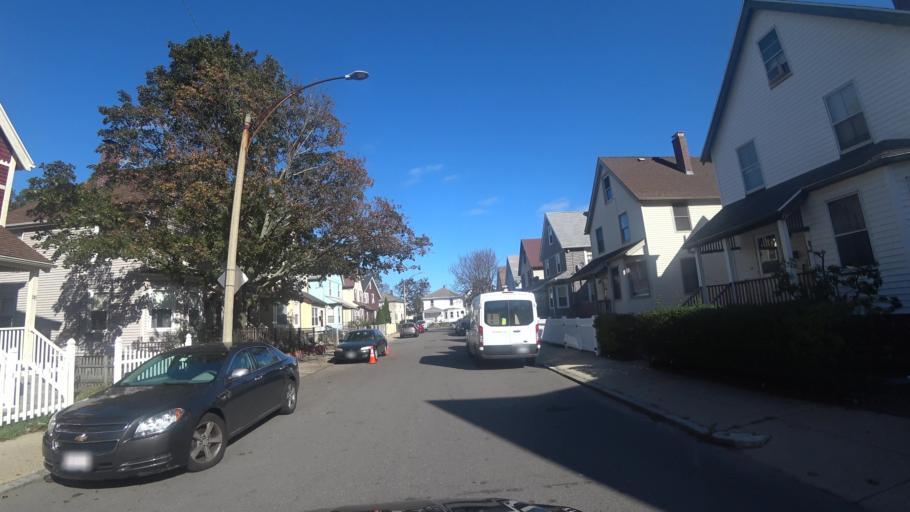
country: US
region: Massachusetts
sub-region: Suffolk County
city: South Boston
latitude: 42.3197
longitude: -71.0643
